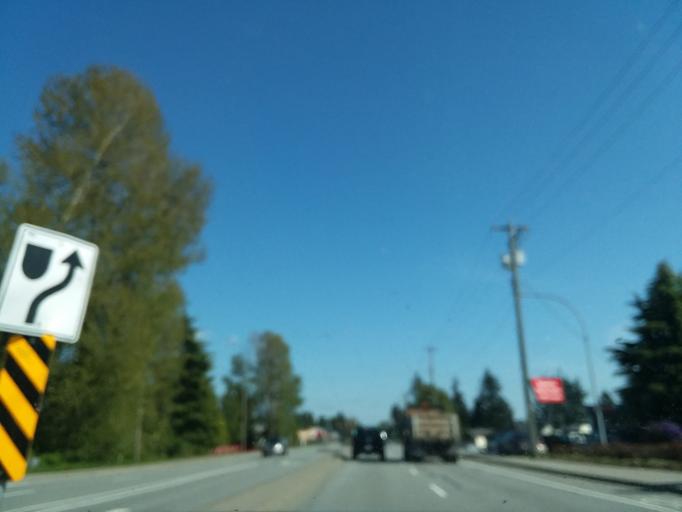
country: CA
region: British Columbia
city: New Westminster
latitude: 49.2434
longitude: -122.8883
